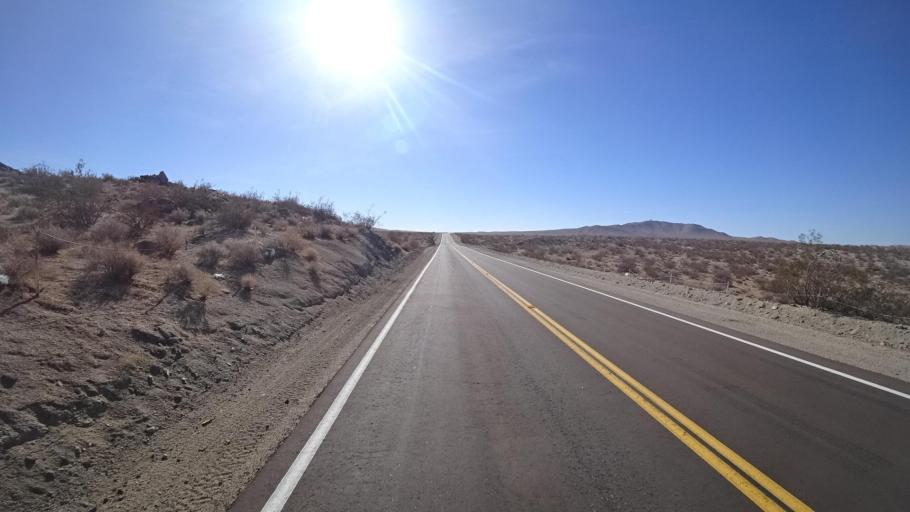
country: US
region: California
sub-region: Kern County
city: Ridgecrest
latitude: 35.4999
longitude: -117.6231
